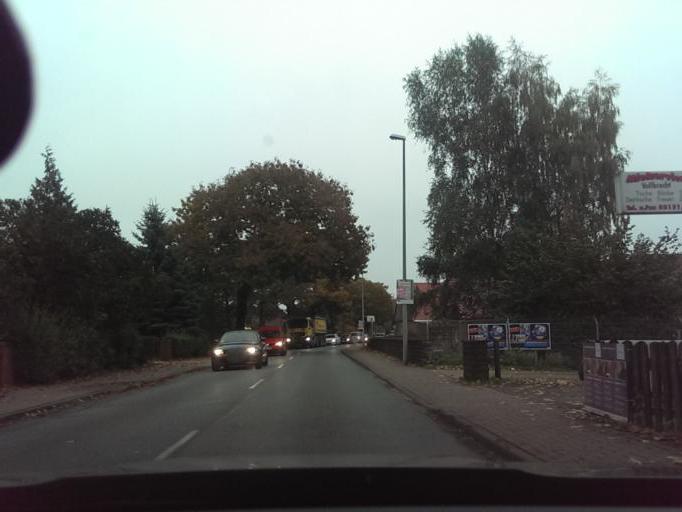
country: DE
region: Lower Saxony
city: Garbsen-Mitte
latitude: 52.4398
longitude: 9.6231
